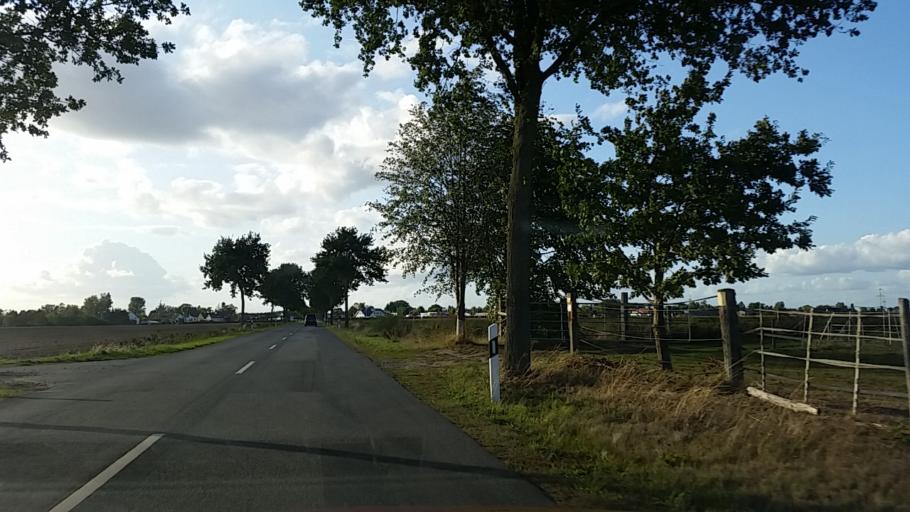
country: DE
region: Lower Saxony
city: Vordorf
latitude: 52.3601
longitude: 10.5322
